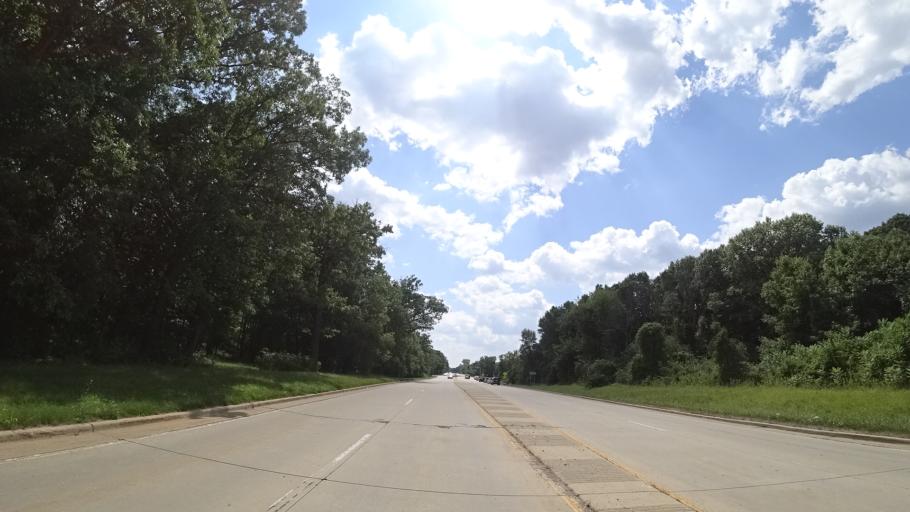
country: US
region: Illinois
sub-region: Cook County
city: Crestwood
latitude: 41.6336
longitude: -87.7766
